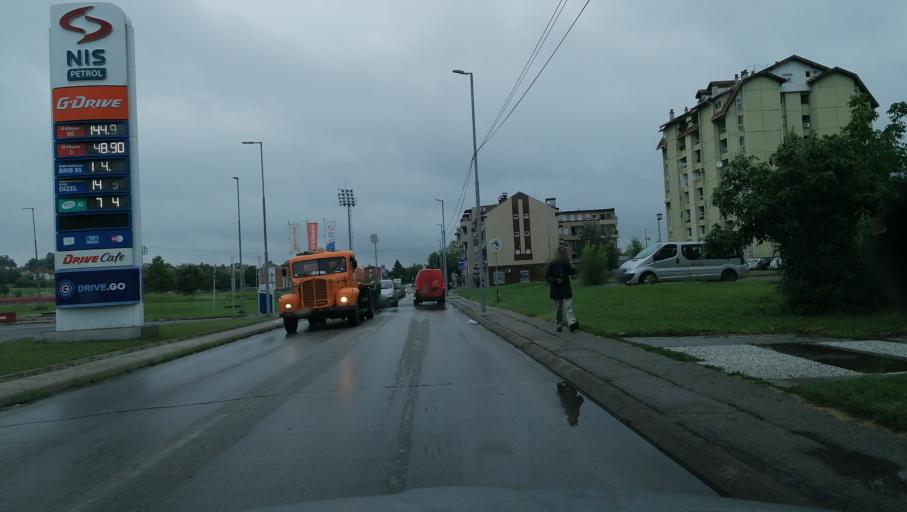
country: RS
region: Central Serbia
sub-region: Rasinski Okrug
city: Krusevac
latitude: 43.5718
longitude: 21.3296
